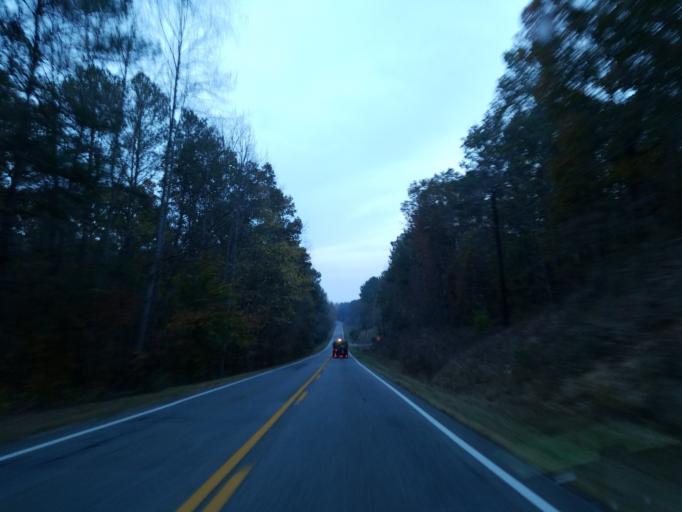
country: US
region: Georgia
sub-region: Pickens County
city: Jasper
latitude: 34.5210
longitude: -84.5698
